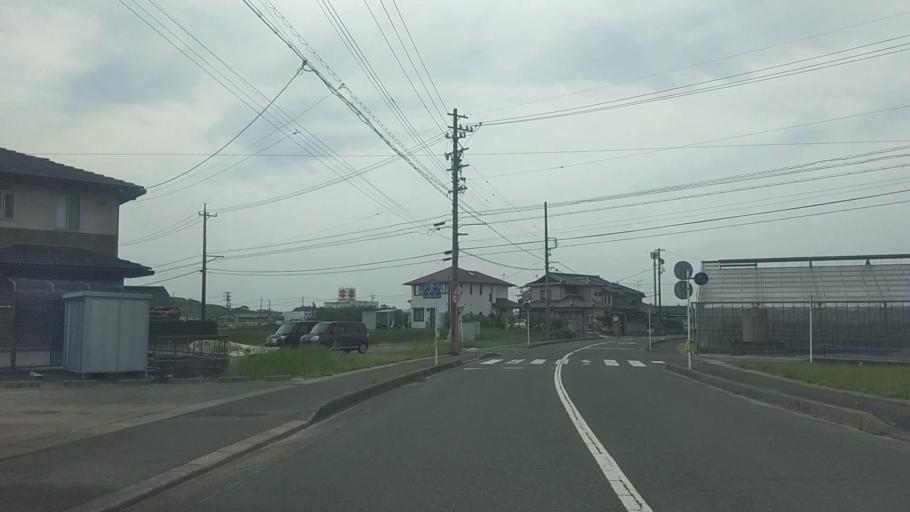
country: JP
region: Shizuoka
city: Kosai-shi
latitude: 34.7302
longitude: 137.5252
